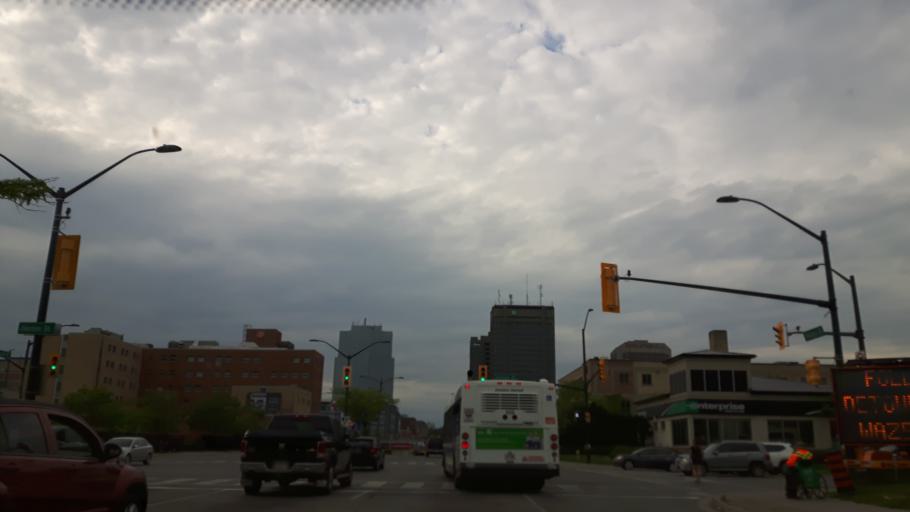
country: CA
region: Ontario
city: London
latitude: 42.9799
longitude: -81.2426
